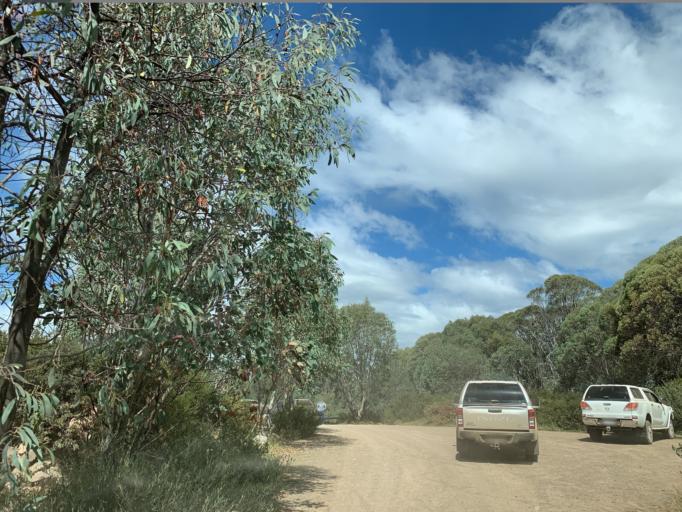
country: AU
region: Victoria
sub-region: Mansfield
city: Mansfield
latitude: -37.1091
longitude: 146.5319
